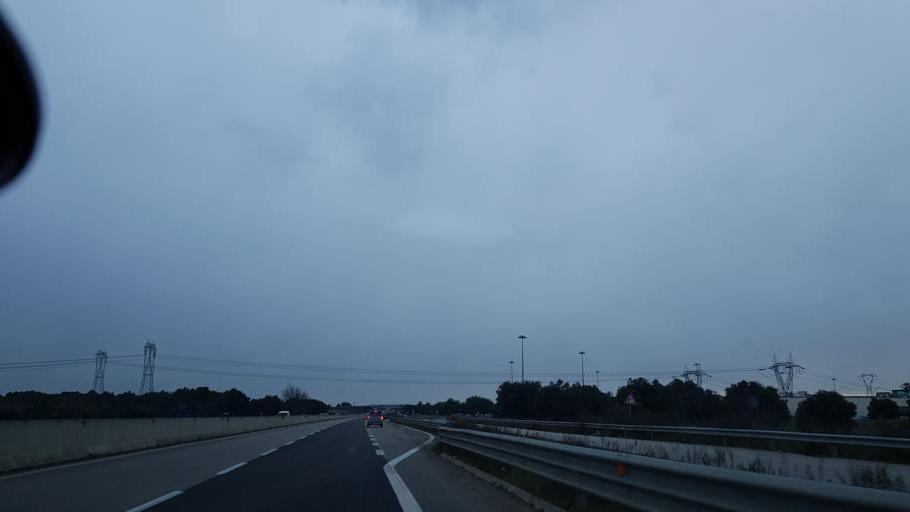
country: IT
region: Apulia
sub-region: Provincia di Brindisi
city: Mesagne
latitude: 40.5803
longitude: 17.8414
